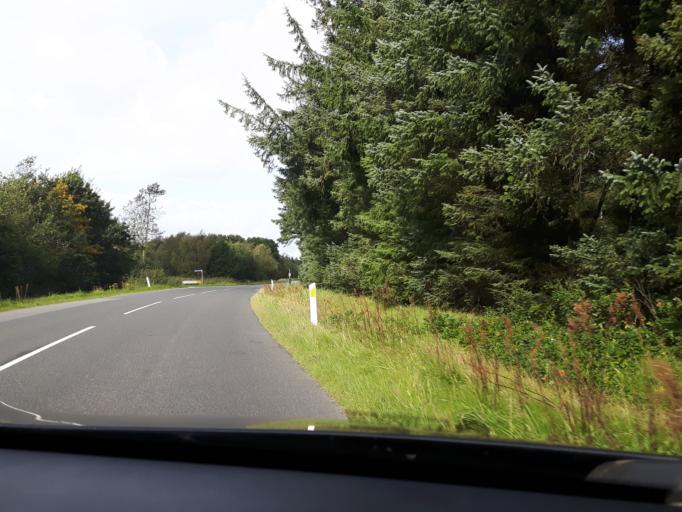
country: DK
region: North Denmark
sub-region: Jammerbugt Kommune
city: Kas
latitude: 57.1880
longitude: 9.5875
